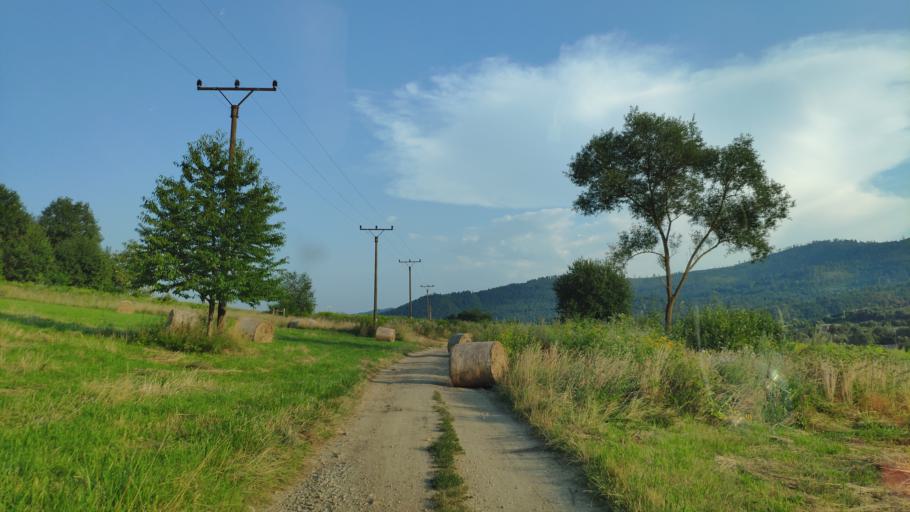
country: SK
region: Kosicky
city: Dobsina
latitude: 48.7183
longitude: 20.2800
